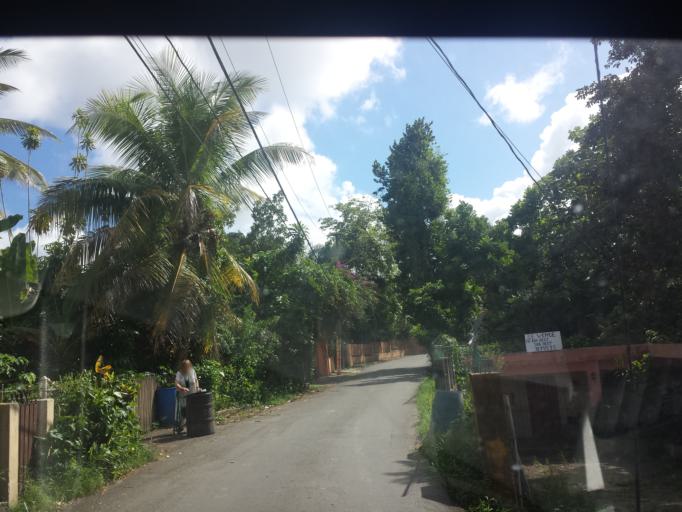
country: PR
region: Trujillo Alto
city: Trujillo Alto
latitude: 18.3465
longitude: -66.0485
